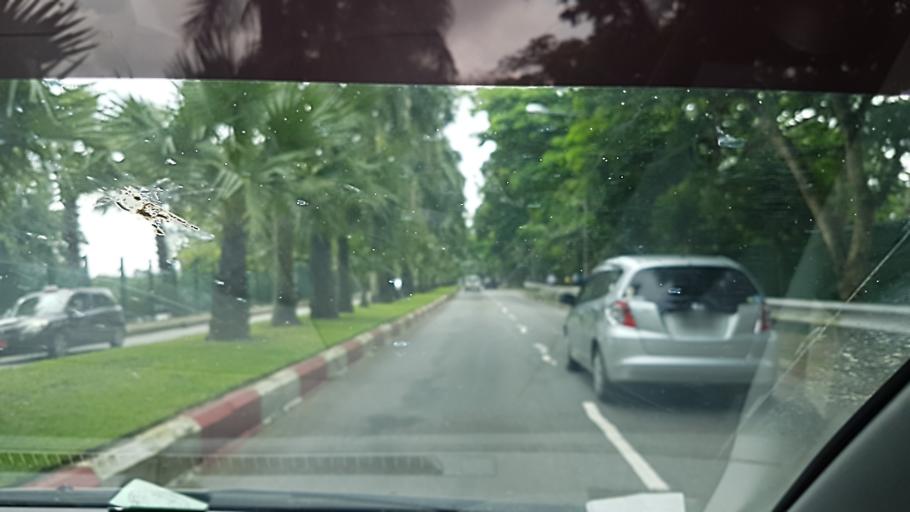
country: MM
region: Yangon
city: Yangon
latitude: 16.7931
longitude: 96.1654
